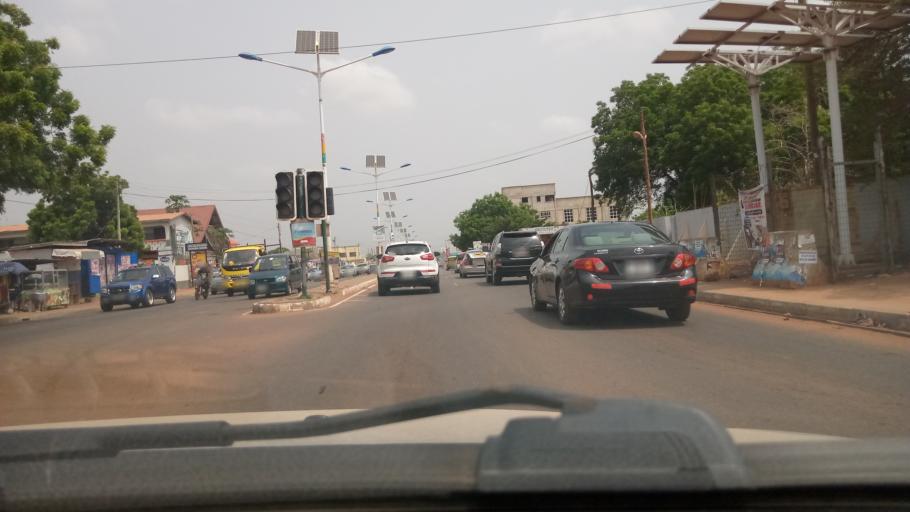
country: GH
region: Greater Accra
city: Medina Estates
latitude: 5.6671
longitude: -0.1515
